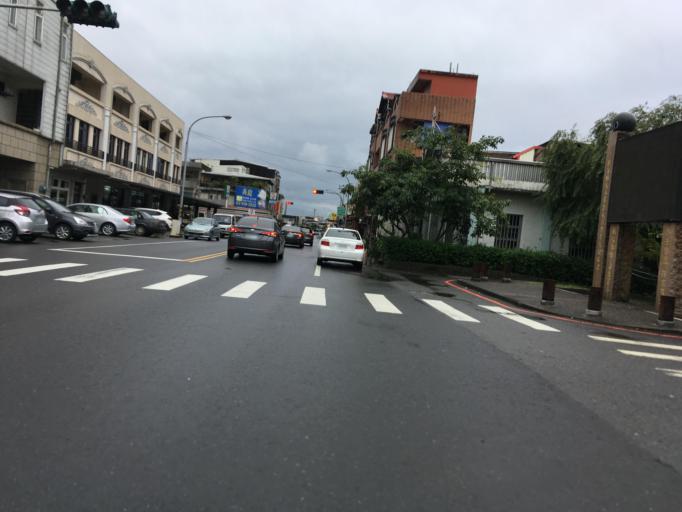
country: TW
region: Taiwan
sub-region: Yilan
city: Yilan
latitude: 24.6551
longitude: 121.7634
